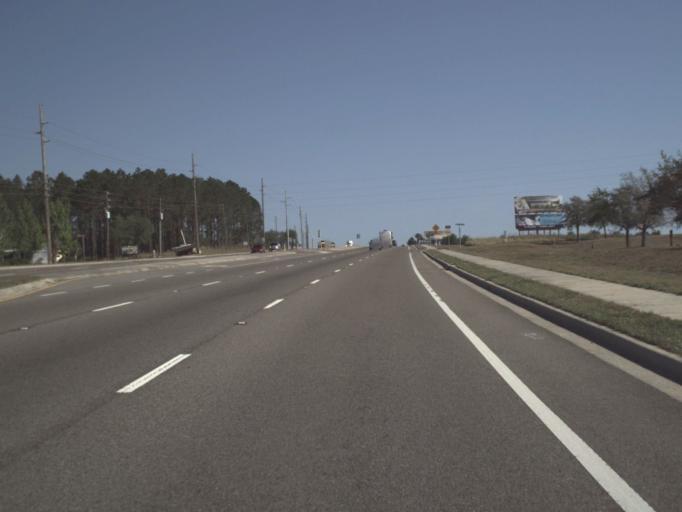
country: US
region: Florida
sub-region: Lake County
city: Minneola
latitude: 28.5854
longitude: -81.7518
